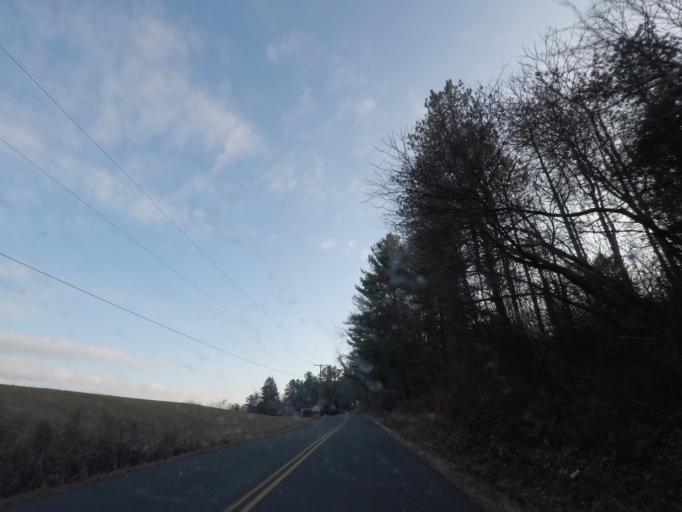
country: US
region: New York
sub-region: Rensselaer County
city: Wynantskill
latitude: 42.7027
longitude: -73.6345
